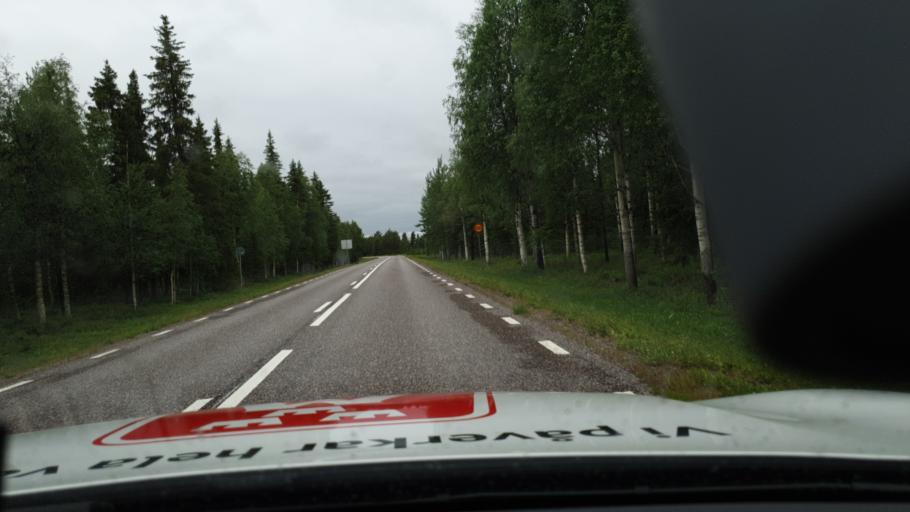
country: SE
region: Norrbotten
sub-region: Pajala Kommun
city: Pajala
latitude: 67.1927
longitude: 23.4674
